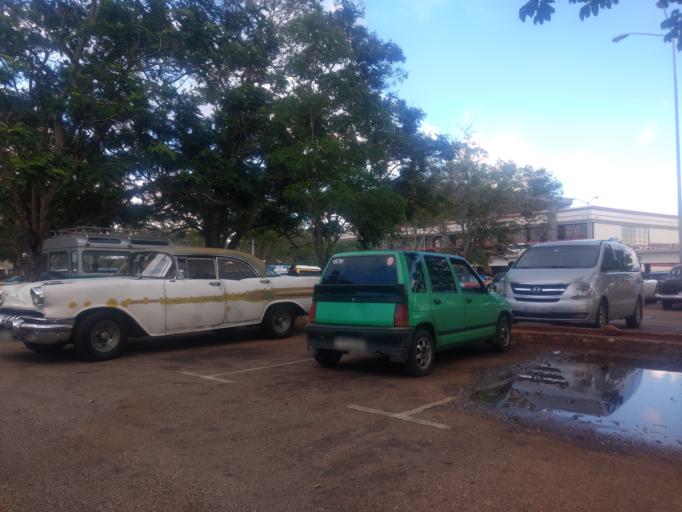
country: CU
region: La Habana
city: Boyeros
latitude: 22.9985
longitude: -82.4095
